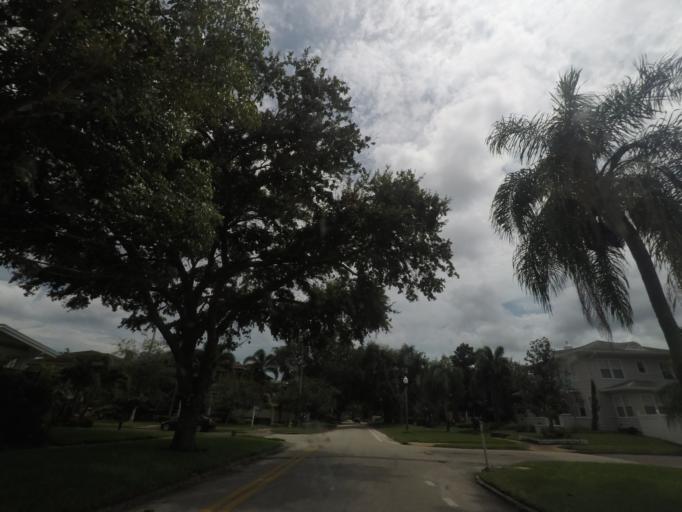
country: US
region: Florida
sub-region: Pinellas County
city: Saint Petersburg
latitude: 27.7860
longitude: -82.6344
